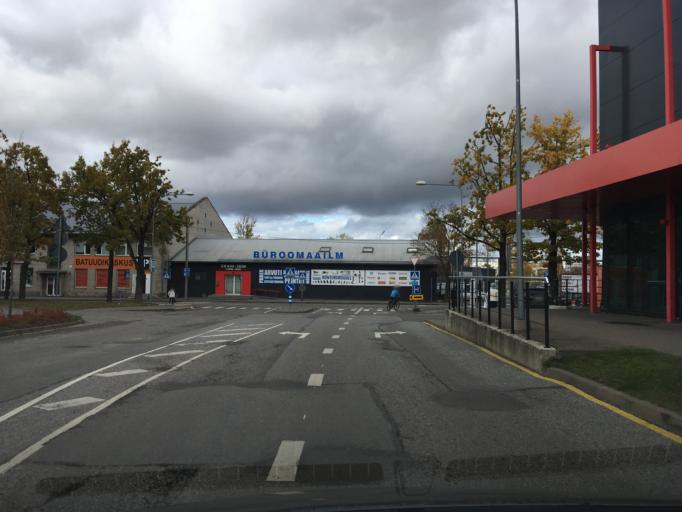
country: EE
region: Paernumaa
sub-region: Paernu linn
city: Parnu
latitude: 58.3875
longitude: 24.5034
